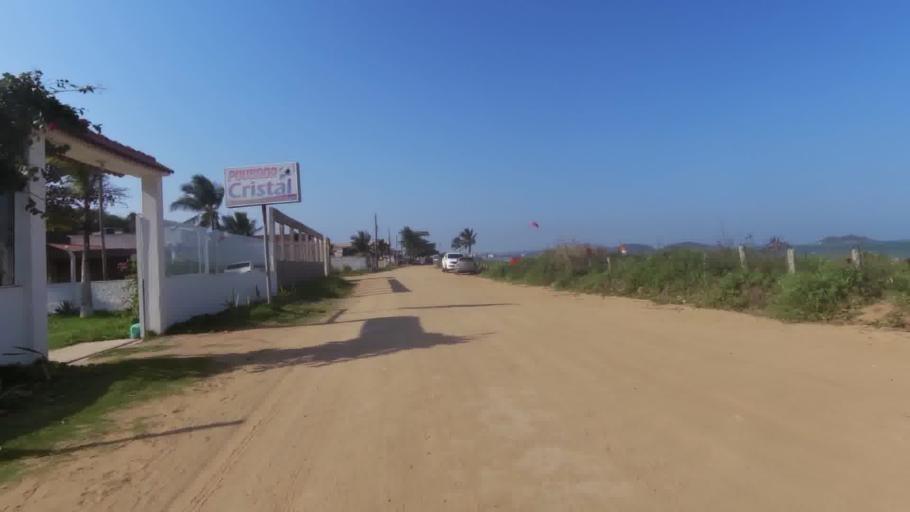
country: BR
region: Espirito Santo
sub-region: Piuma
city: Piuma
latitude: -20.8566
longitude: -40.7529
